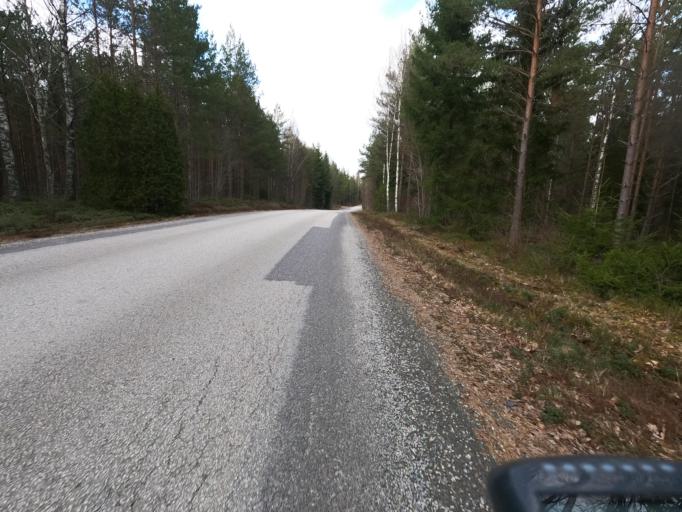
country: SE
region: Kronoberg
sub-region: Alvesta Kommun
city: Vislanda
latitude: 56.8047
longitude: 14.4887
